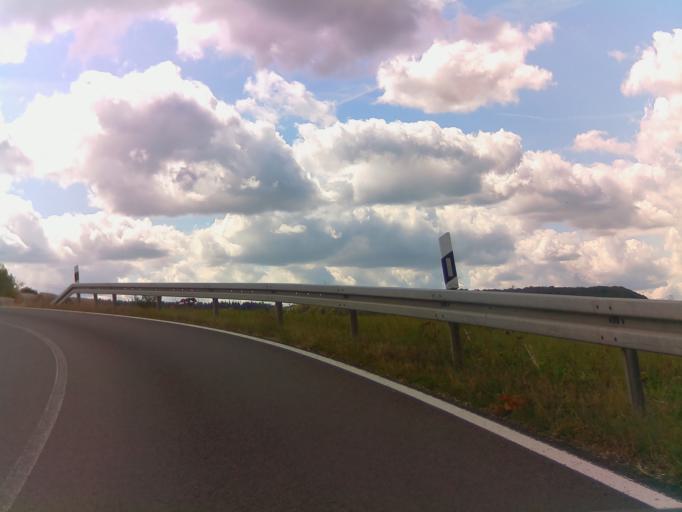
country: DE
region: Thuringia
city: Dillstadt
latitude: 50.5778
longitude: 10.5366
